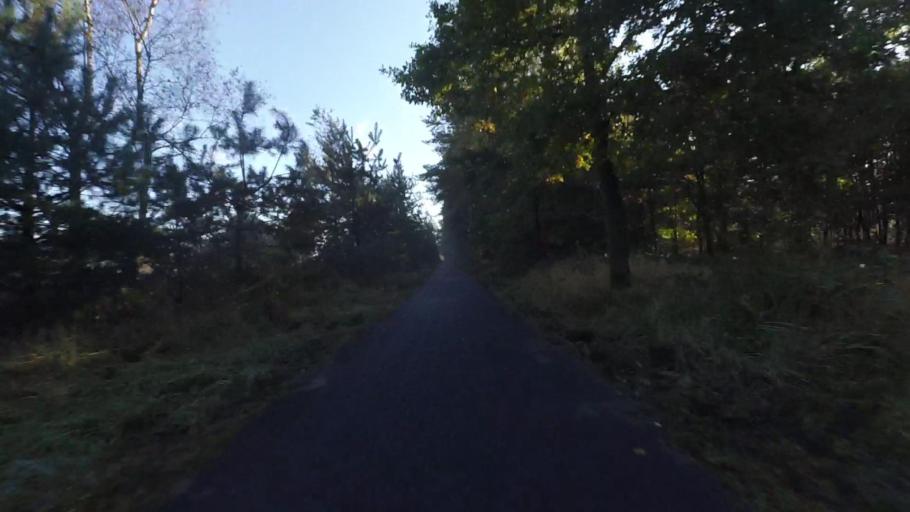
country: NL
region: Gelderland
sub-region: Gemeente Epe
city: Emst
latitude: 52.3170
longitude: 5.9062
